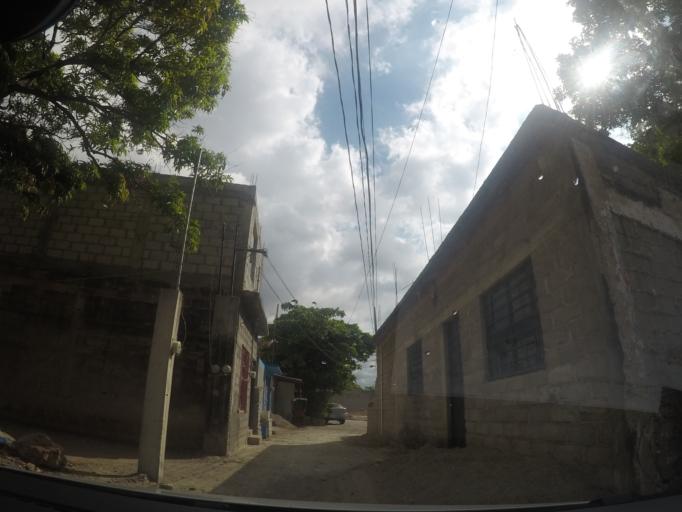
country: MX
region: Oaxaca
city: Juchitan de Zaragoza
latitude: 16.4300
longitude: -95.0296
